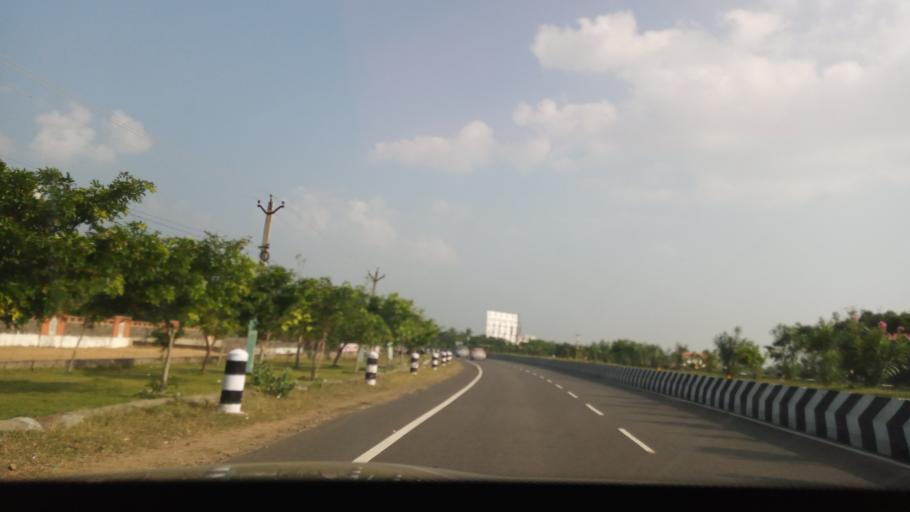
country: IN
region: Tamil Nadu
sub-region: Kancheepuram
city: Injambakkam
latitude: 12.7721
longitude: 80.2486
